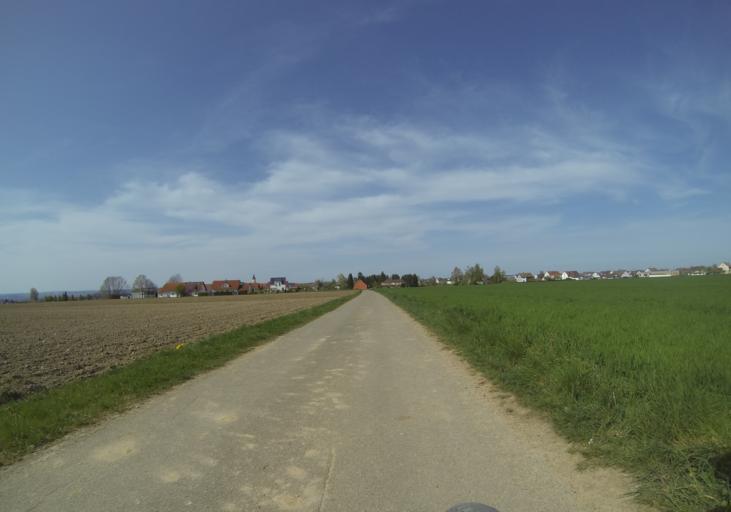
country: DE
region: Baden-Wuerttemberg
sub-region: Tuebingen Region
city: Burgrieden
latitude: 48.2562
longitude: 9.9284
